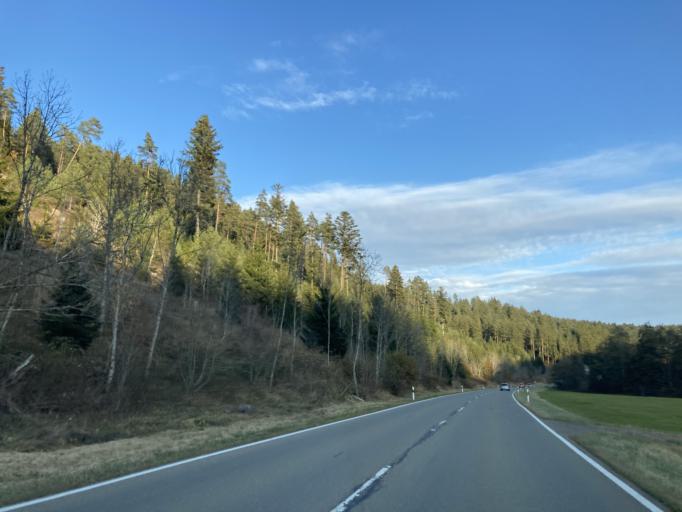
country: DE
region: Baden-Wuerttemberg
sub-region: Freiburg Region
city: Unterkirnach
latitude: 47.9903
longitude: 8.3697
